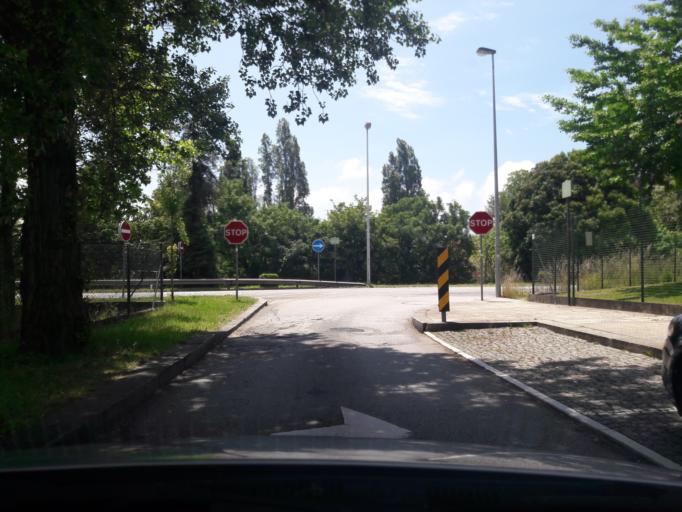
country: PT
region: Porto
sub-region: Porto
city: Porto
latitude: 41.1518
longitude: -8.6346
